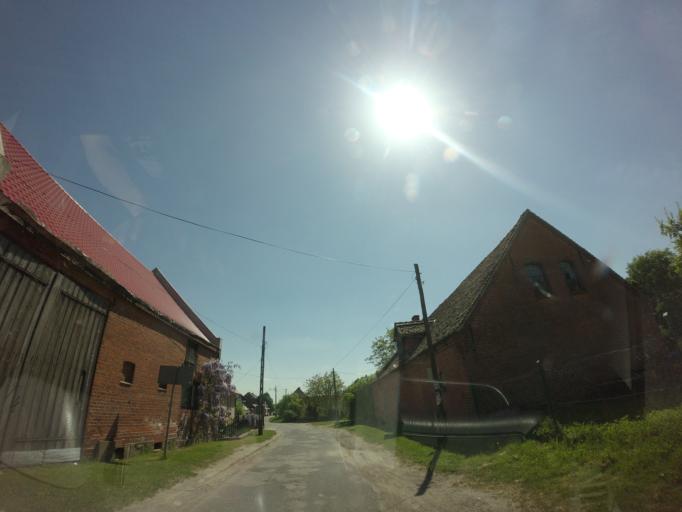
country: PL
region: West Pomeranian Voivodeship
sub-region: Powiat mysliborski
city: Nowogrodek Pomorski
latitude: 52.9124
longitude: 15.0271
